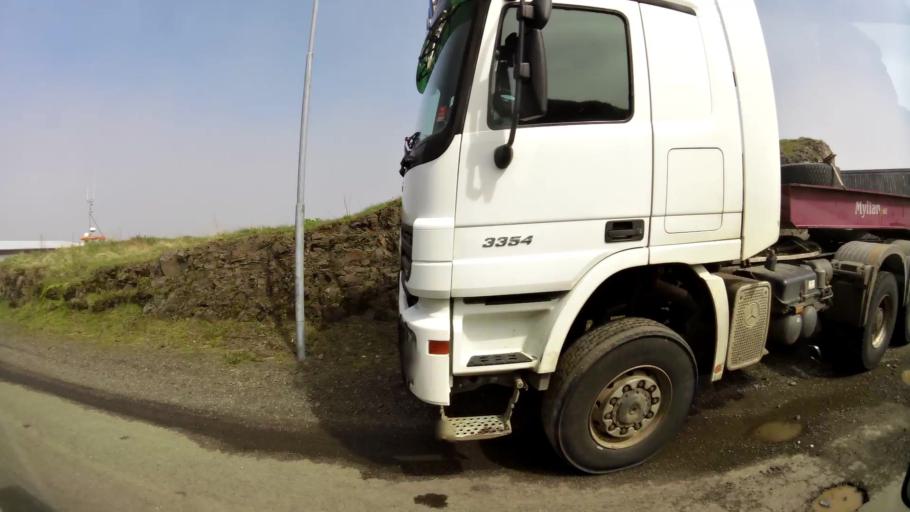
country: IS
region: East
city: Reydarfjoerdur
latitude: 64.6576
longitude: -14.2840
